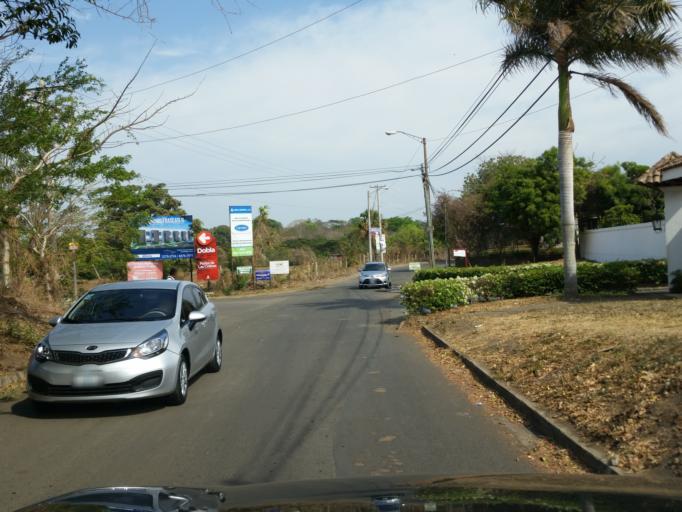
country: NI
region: Managua
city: Managua
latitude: 12.0876
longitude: -86.2210
